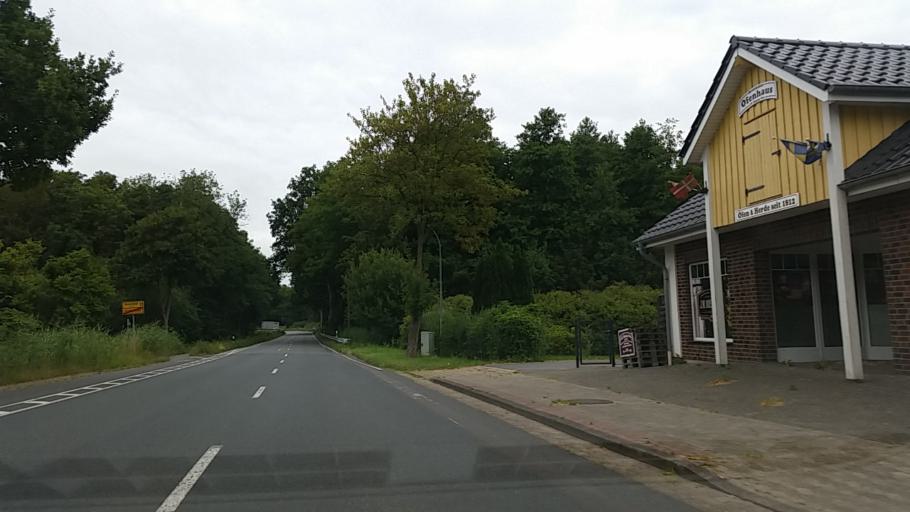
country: DE
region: Lower Saxony
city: Beverstedt
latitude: 53.4245
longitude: 8.8892
